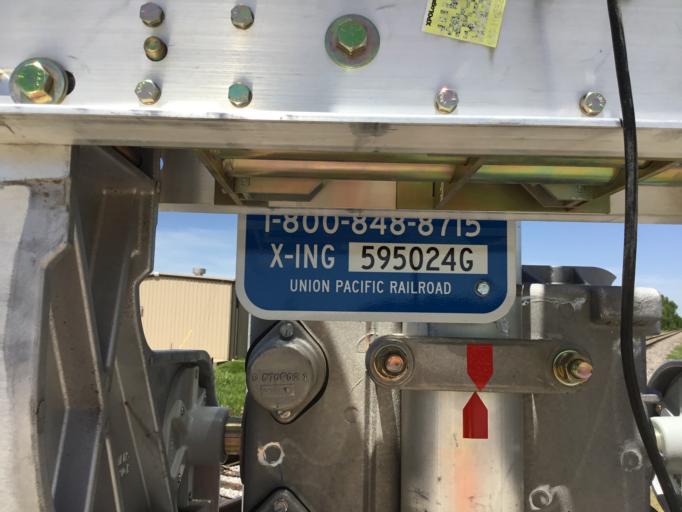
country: US
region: Kansas
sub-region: Sedgwick County
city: Bellaire
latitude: 37.7668
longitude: -97.2974
